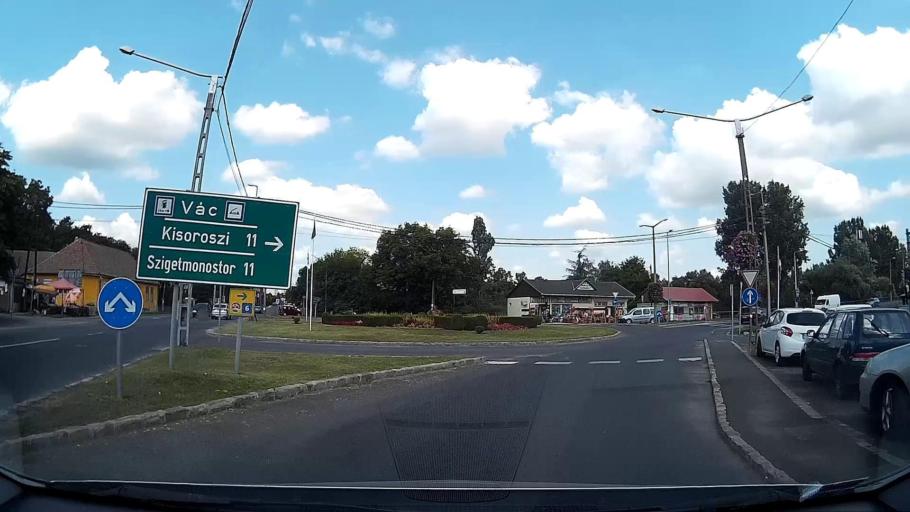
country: HU
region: Pest
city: Tahitotfalu
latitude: 47.7512
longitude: 19.0768
